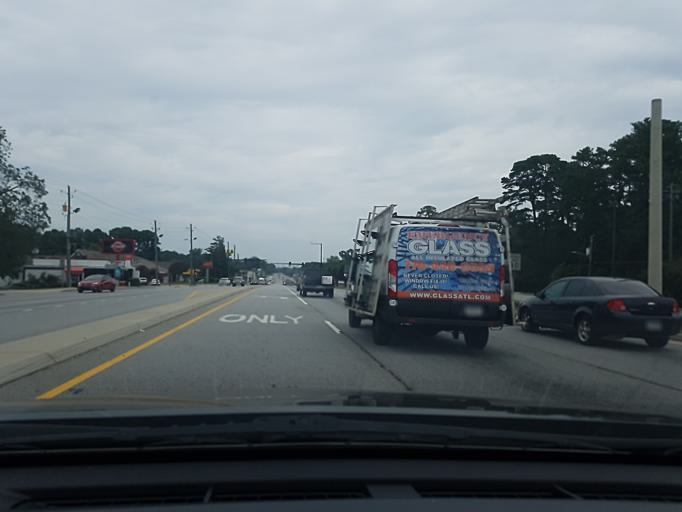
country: US
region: Georgia
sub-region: Clayton County
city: Morrow
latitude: 33.5792
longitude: -84.3405
